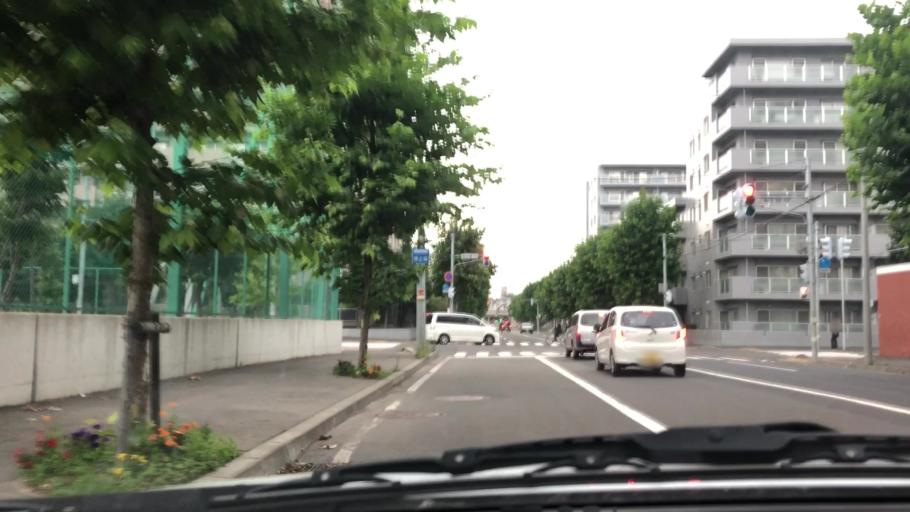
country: JP
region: Hokkaido
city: Sapporo
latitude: 43.0682
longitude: 141.3291
